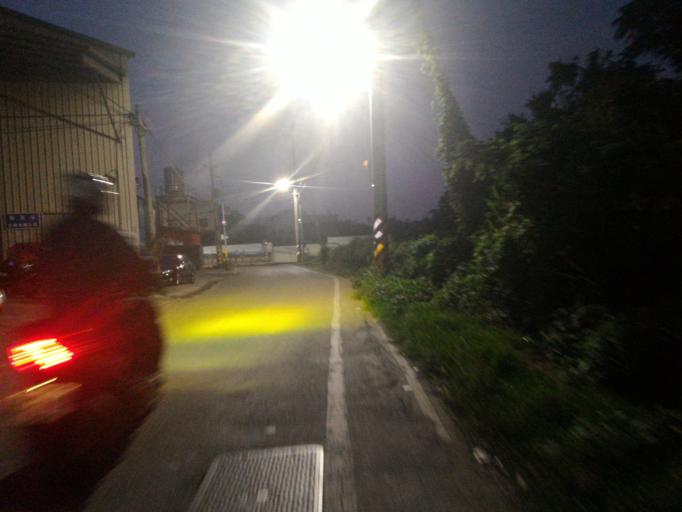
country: TW
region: Taipei
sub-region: Taipei
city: Banqiao
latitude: 24.9618
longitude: 121.4093
